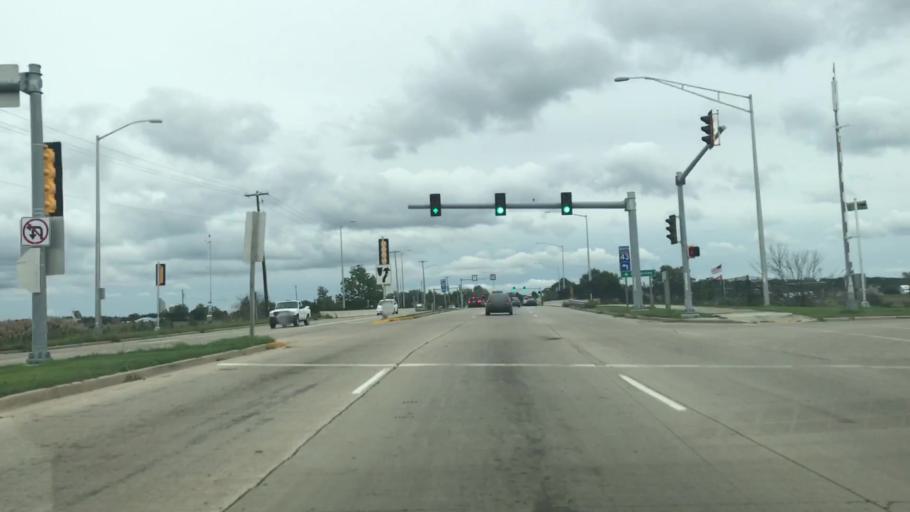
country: US
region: Wisconsin
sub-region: Waukesha County
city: Mukwonago
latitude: 42.8525
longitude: -88.3228
